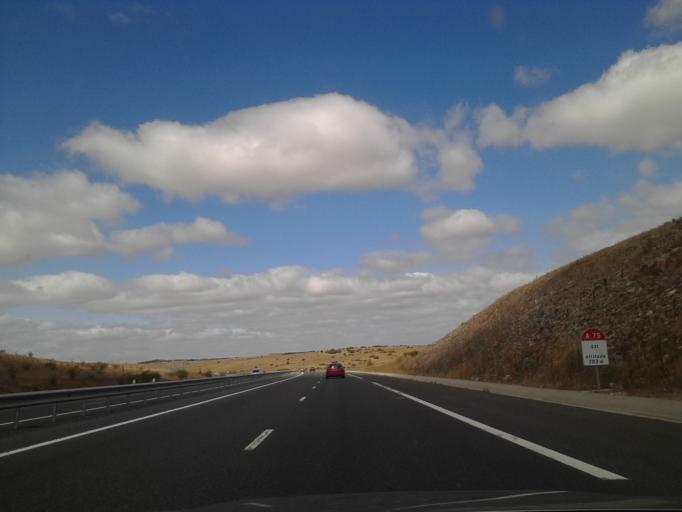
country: FR
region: Midi-Pyrenees
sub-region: Departement de l'Aveyron
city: La Cavalerie
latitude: 44.0284
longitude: 3.1031
